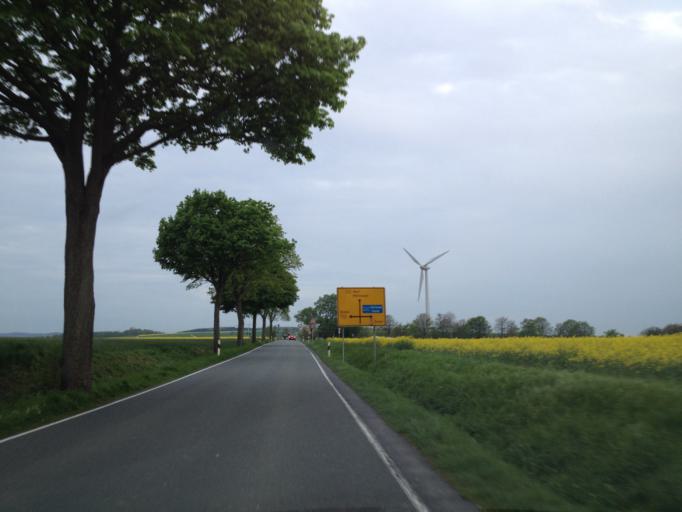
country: DE
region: North Rhine-Westphalia
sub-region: Regierungsbezirk Arnsberg
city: Mohnesee
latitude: 51.5057
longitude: 8.2027
